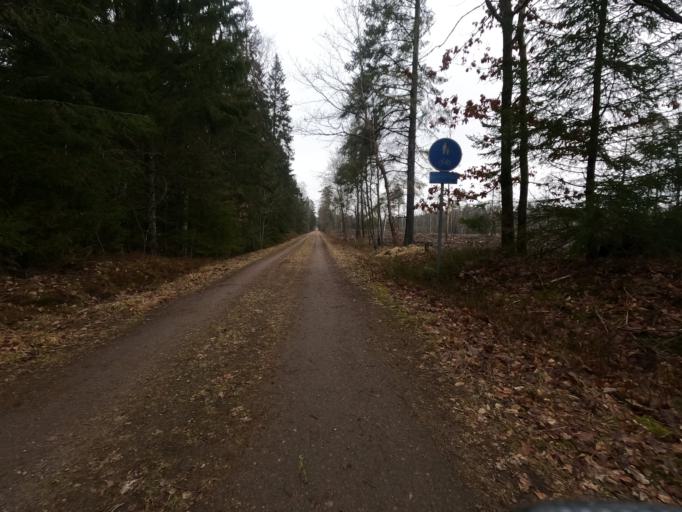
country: SE
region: Kronoberg
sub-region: Markaryds Kommun
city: Stromsnasbruk
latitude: 56.7913
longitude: 13.6646
